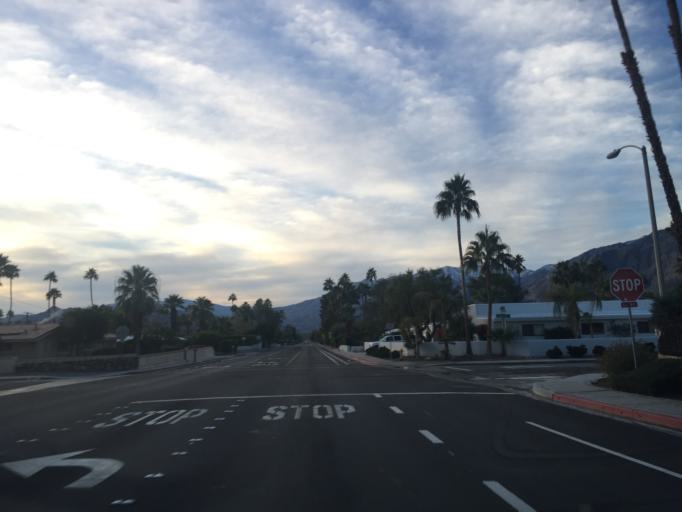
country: US
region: California
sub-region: Riverside County
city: Palm Springs
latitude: 33.8401
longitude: -116.5369
